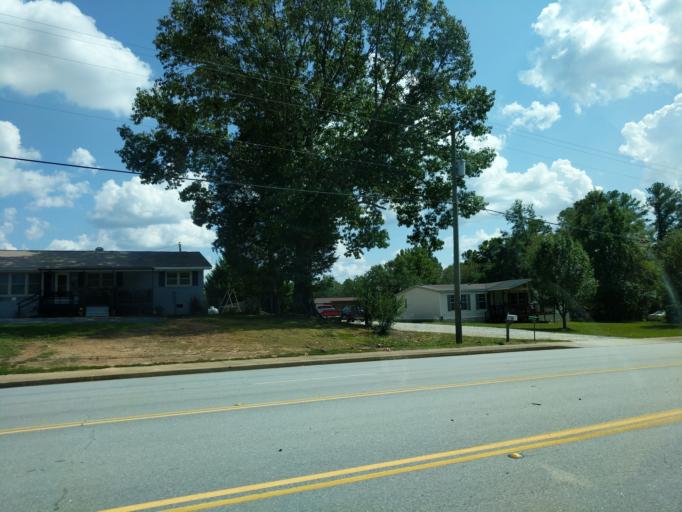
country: US
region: South Carolina
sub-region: Spartanburg County
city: Woodruff
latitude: 34.7637
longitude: -82.0341
